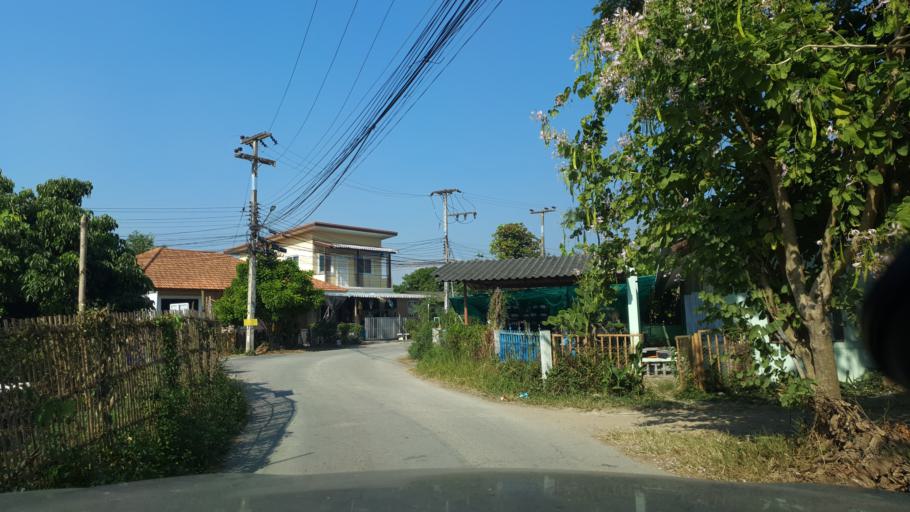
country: TH
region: Chiang Mai
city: Saraphi
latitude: 18.7185
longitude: 99.0715
